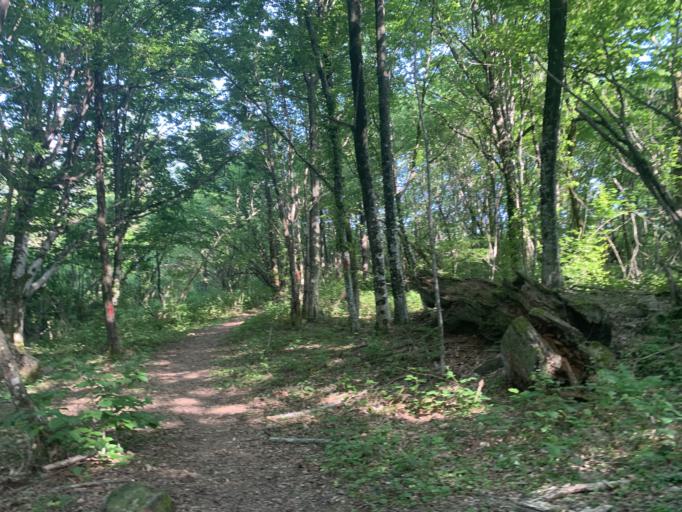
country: RU
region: Krasnodarskiy
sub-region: Sochi City
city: Lazarevskoye
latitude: 43.9515
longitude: 39.3277
